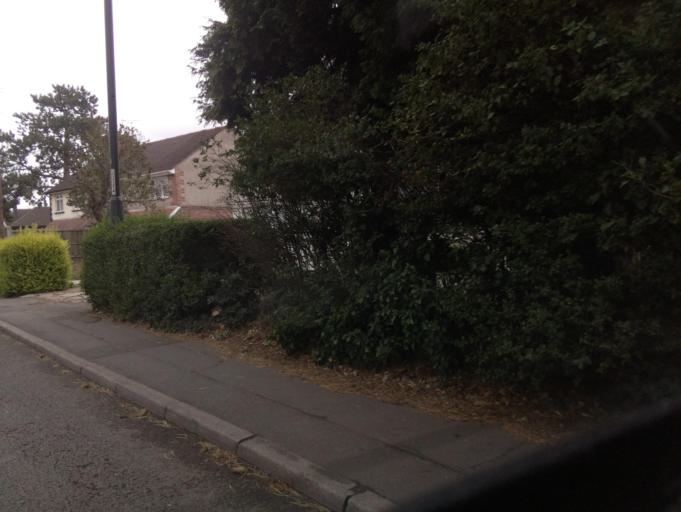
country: GB
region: England
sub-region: Derby
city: Derby
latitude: 52.8969
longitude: -1.5102
